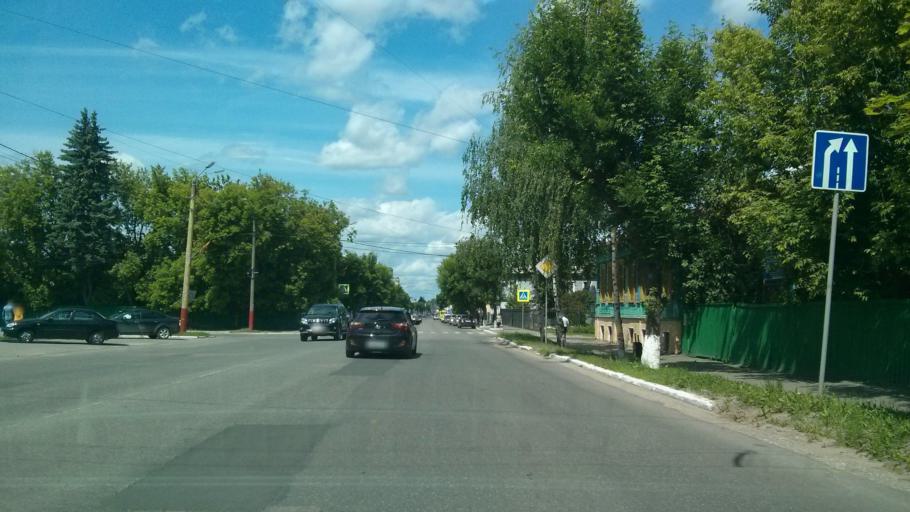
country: RU
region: Vladimir
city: Murom
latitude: 55.5749
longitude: 42.0555
